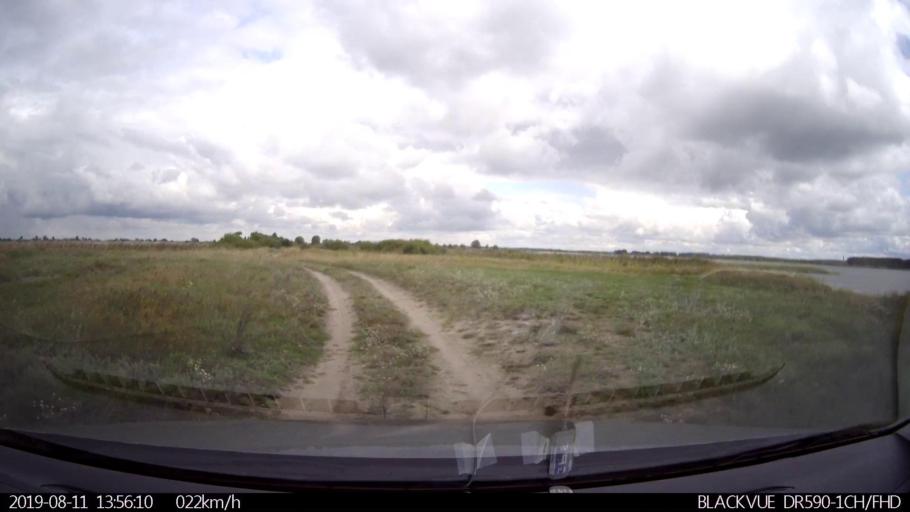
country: RU
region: Ulyanovsk
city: Ignatovka
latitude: 53.8470
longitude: 47.5881
